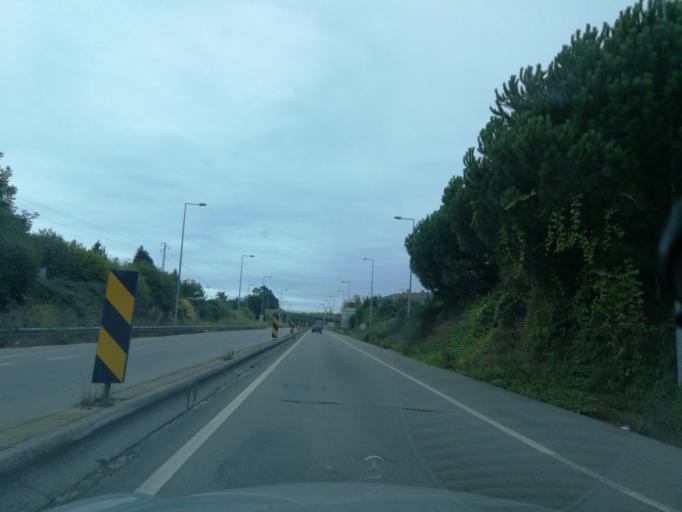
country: PT
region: Aveiro
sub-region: Agueda
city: Valongo
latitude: 40.6105
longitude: -8.4656
